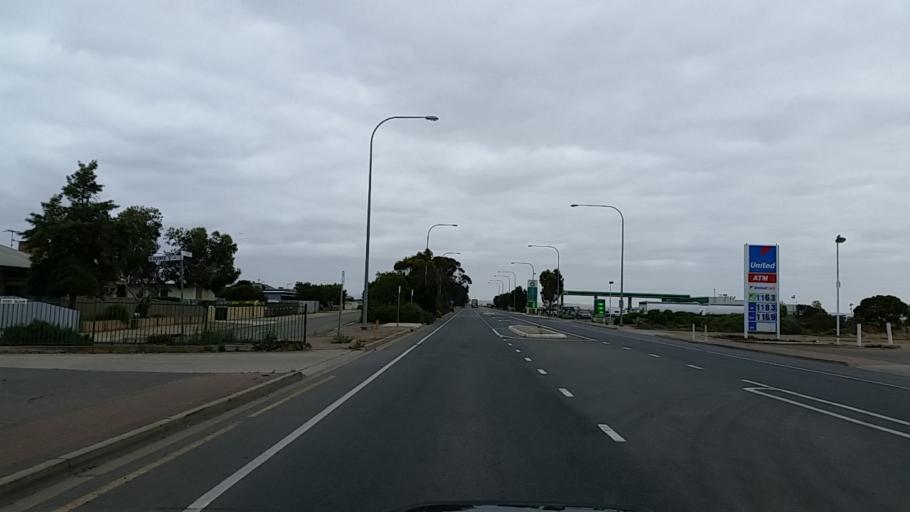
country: AU
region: South Australia
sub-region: Wakefield
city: Balaklava
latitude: -34.1824
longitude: 138.1536
